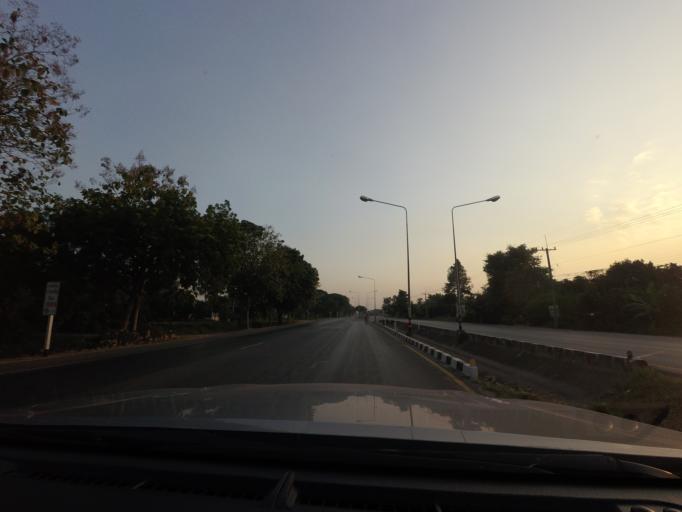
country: TH
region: Phitsanulok
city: Wang Thong
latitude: 16.7310
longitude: 100.4316
